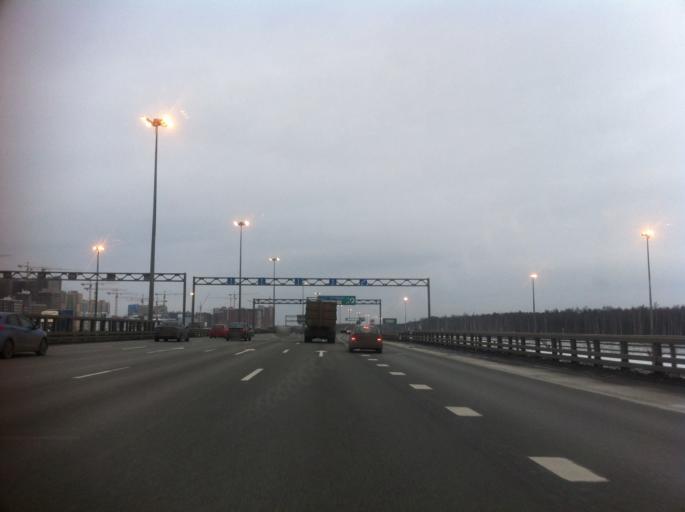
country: RU
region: Leningrad
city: Rybatskoye
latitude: 59.8833
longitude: 30.5270
